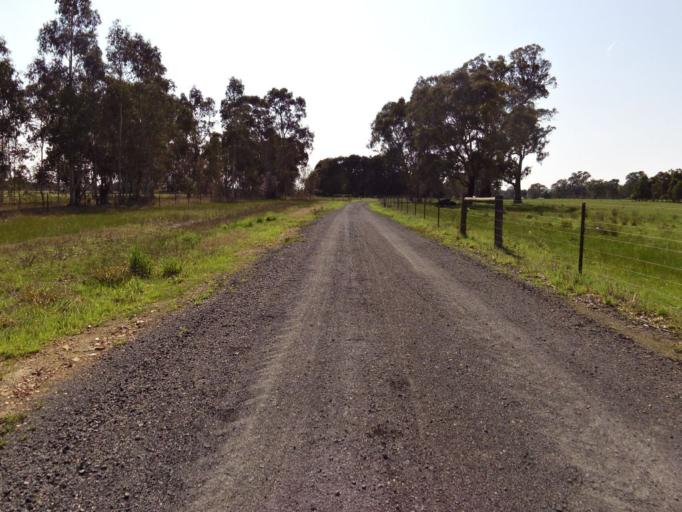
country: AU
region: Victoria
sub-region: Murrindindi
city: Alexandra
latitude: -37.1126
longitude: 145.6088
